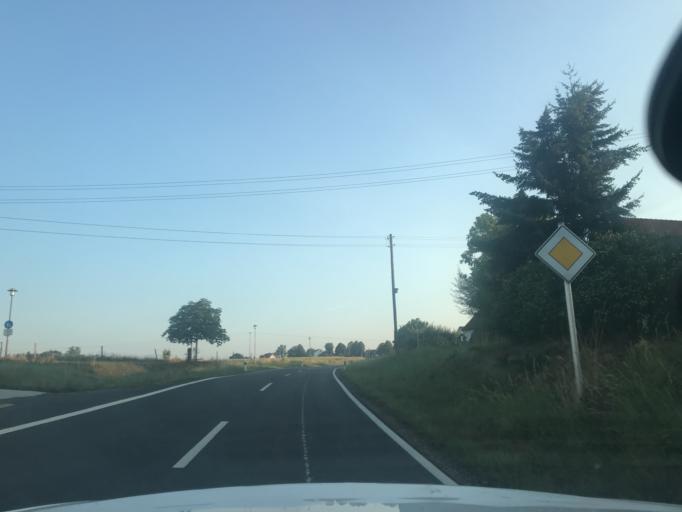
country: DE
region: Bavaria
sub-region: Upper Franconia
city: Pegnitz
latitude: 49.7099
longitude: 11.5761
